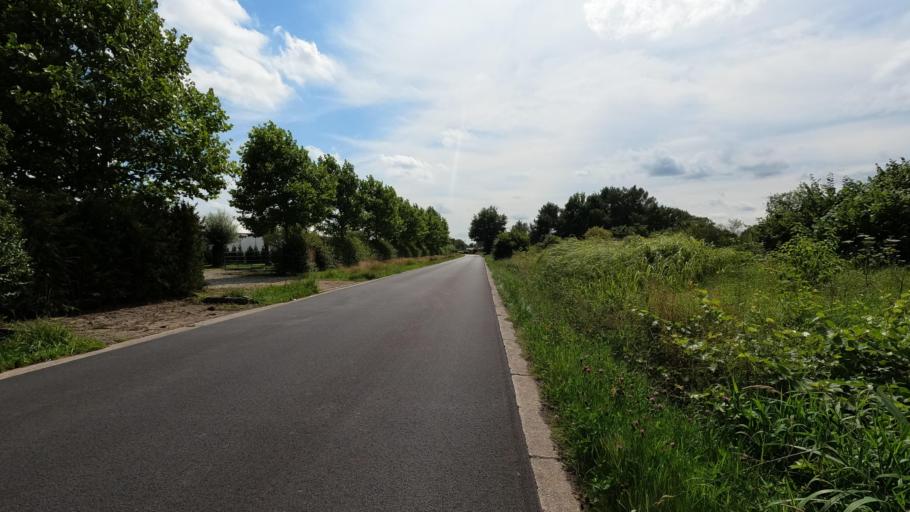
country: BE
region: Flanders
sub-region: Provincie Vlaams-Brabant
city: Begijnendijk
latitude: 51.0405
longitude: 4.7880
